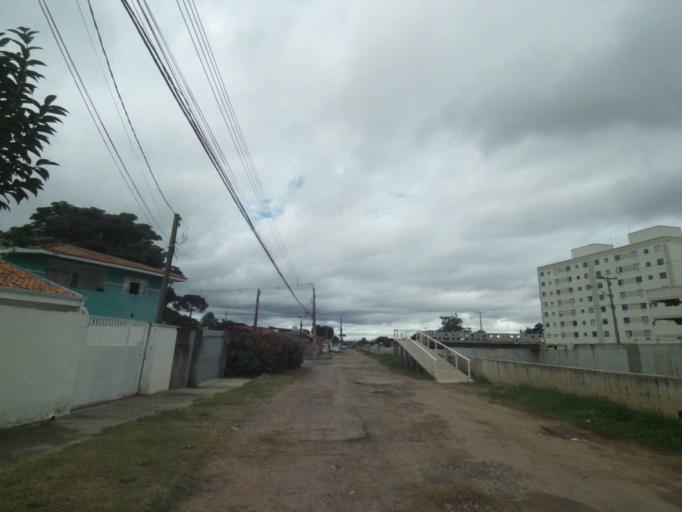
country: BR
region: Parana
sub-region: Curitiba
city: Curitiba
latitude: -25.4796
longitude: -49.2726
